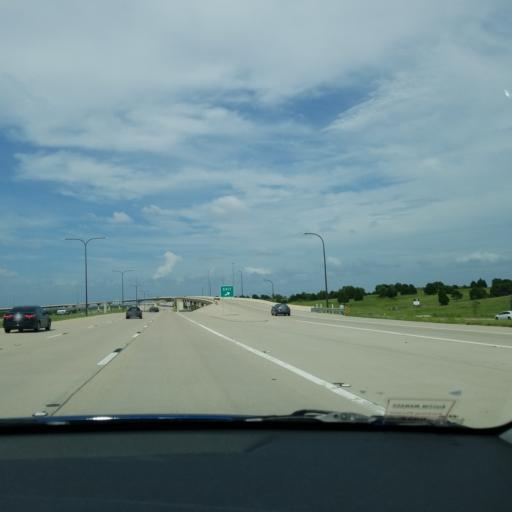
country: US
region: Texas
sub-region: Travis County
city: Manor
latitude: 30.3363
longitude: -97.6023
